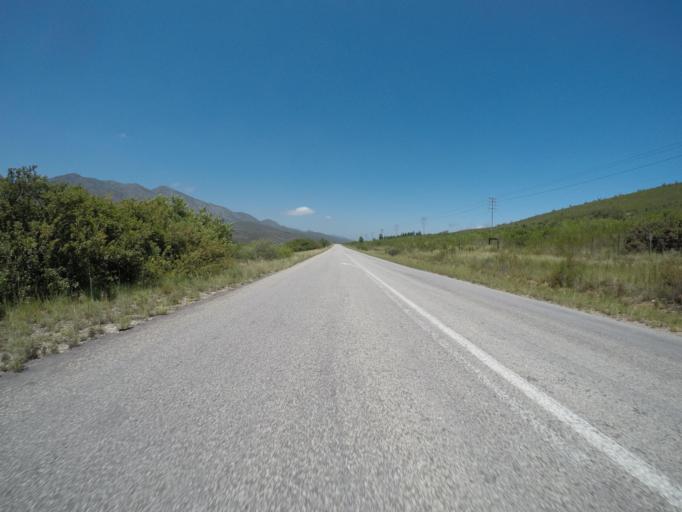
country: ZA
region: Eastern Cape
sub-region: Cacadu District Municipality
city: Kareedouw
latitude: -33.9068
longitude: 24.1523
